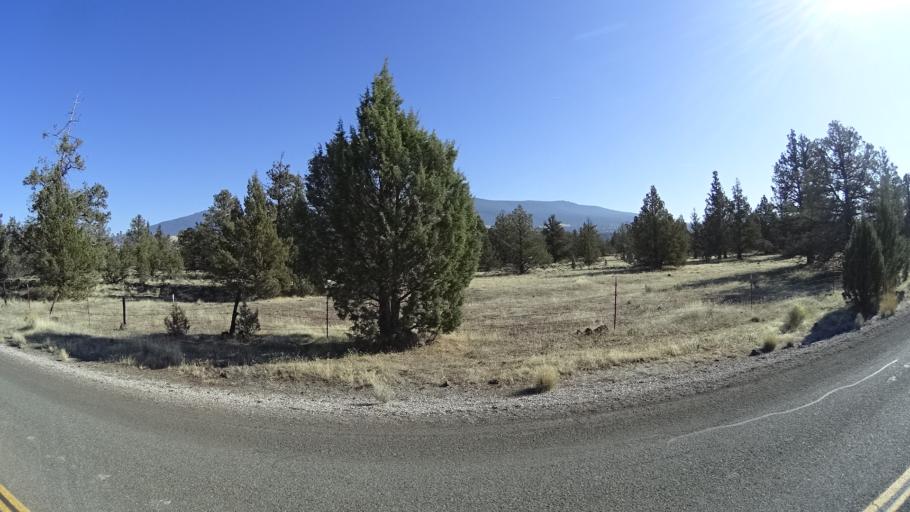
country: US
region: California
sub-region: Siskiyou County
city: Montague
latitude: 41.6502
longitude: -122.3599
